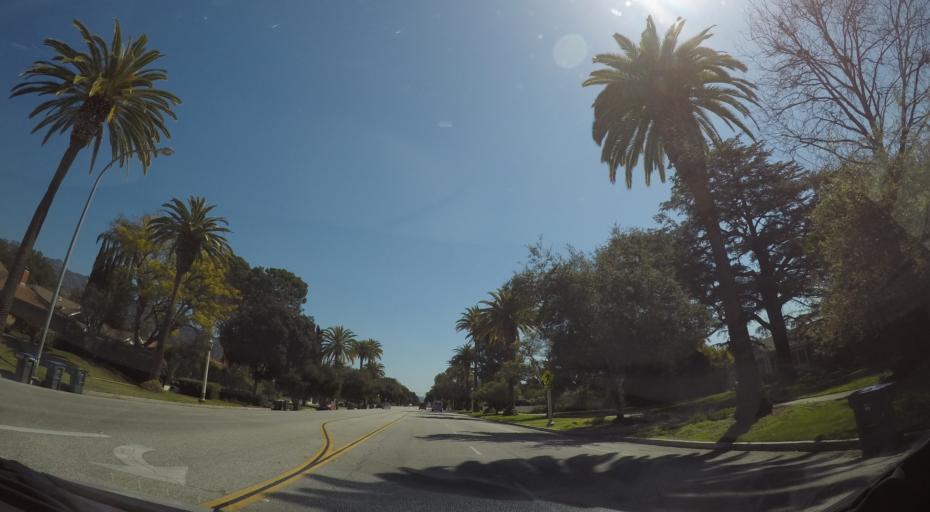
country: US
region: California
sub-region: Los Angeles County
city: Pasadena
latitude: 34.1578
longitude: -118.1196
